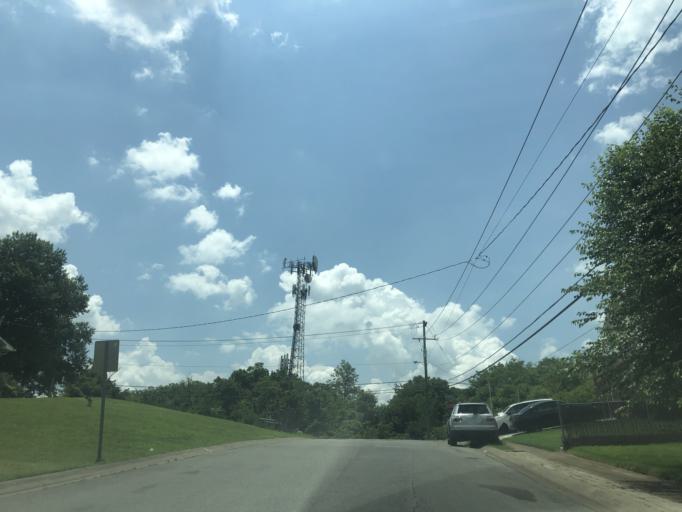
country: US
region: Tennessee
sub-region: Rutherford County
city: La Vergne
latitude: 36.0553
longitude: -86.6602
